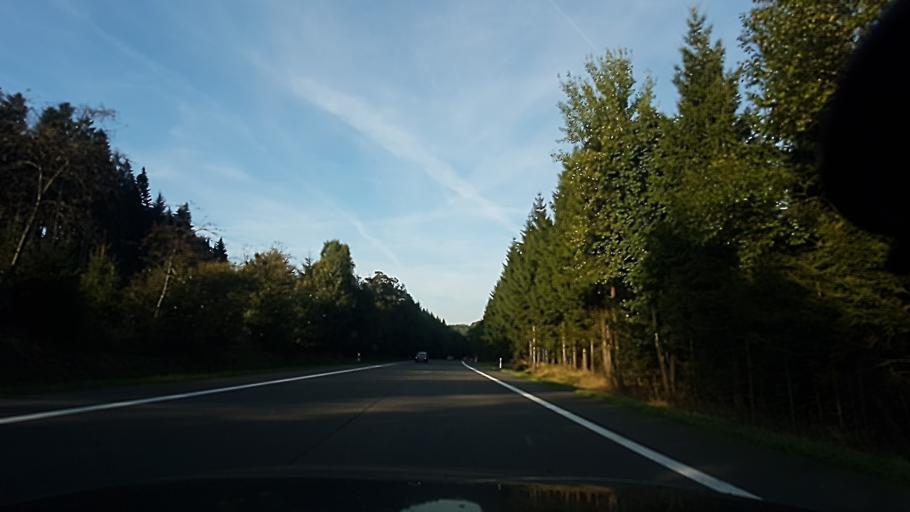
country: DE
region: North Rhine-Westphalia
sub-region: Regierungsbezirk Koln
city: Marienheide
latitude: 51.0831
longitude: 7.5783
